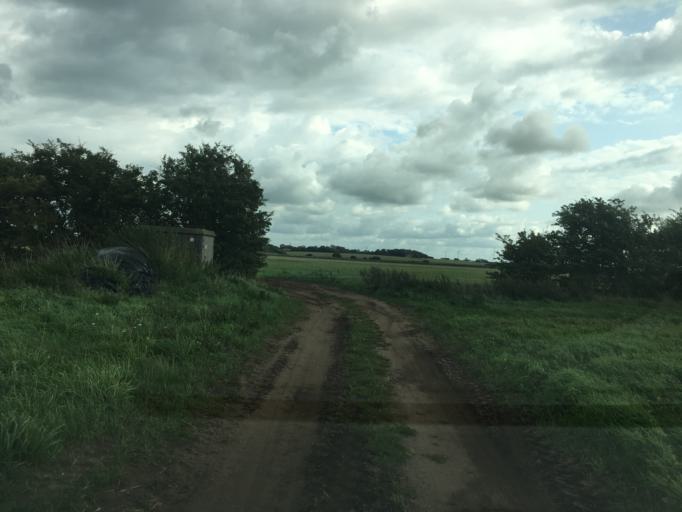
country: DK
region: South Denmark
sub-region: Tonder Kommune
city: Tonder
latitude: 54.9438
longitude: 8.9078
